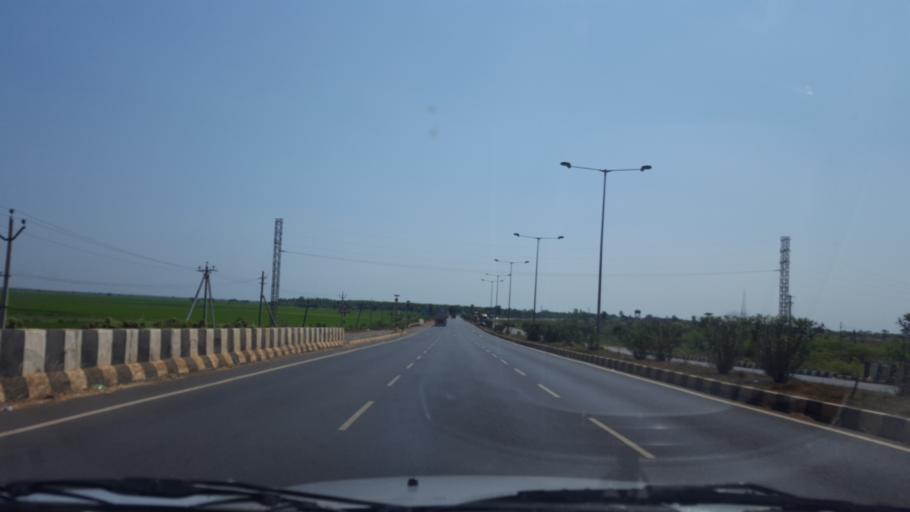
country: IN
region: Andhra Pradesh
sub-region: Nellore
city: Kavali
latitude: 14.7758
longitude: 80.0015
